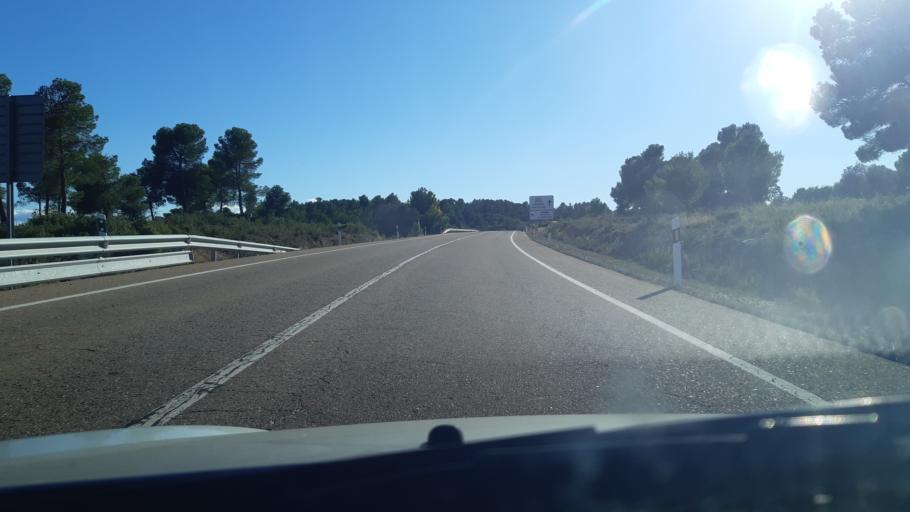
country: ES
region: Aragon
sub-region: Provincia de Teruel
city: Fornoles
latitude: 40.9177
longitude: -0.0189
